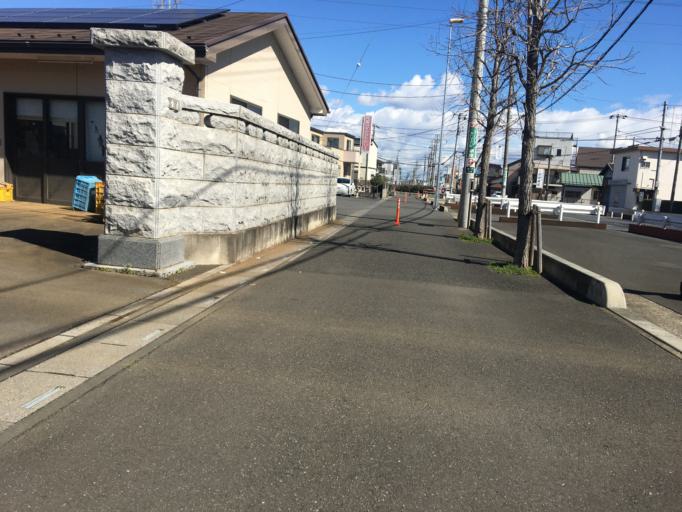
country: JP
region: Saitama
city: Shiki
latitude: 35.7931
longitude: 139.5518
